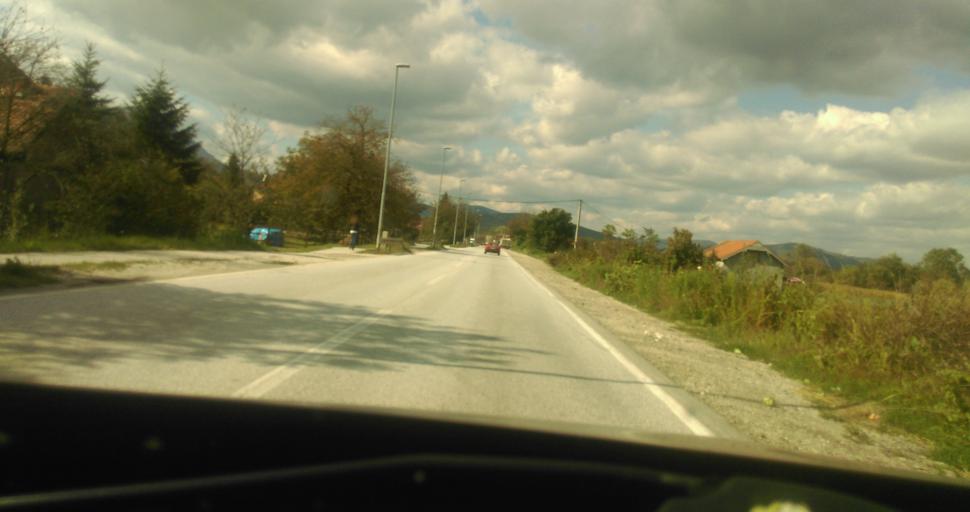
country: RS
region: Central Serbia
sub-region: Moravicki Okrug
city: Cacak
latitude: 43.8942
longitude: 20.3013
